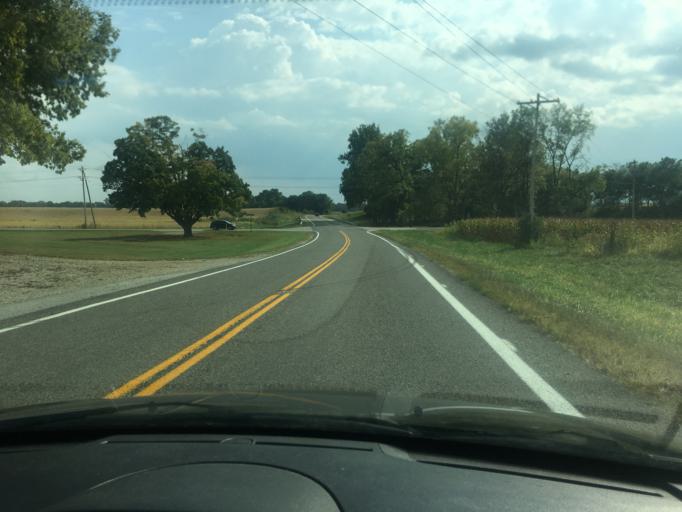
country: US
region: Ohio
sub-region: Champaign County
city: Urbana
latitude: 40.1324
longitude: -83.8355
